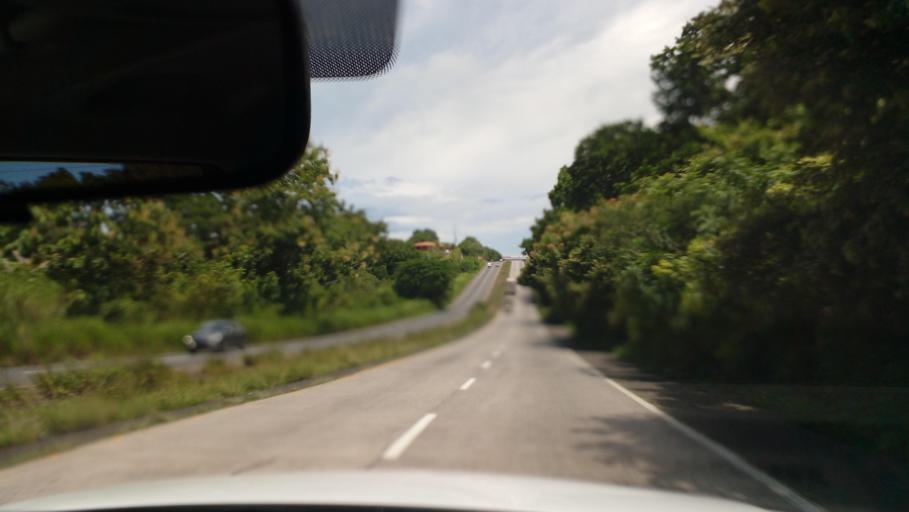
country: PA
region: Panama
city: Nueva Gorgona
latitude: 8.4937
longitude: -79.9582
